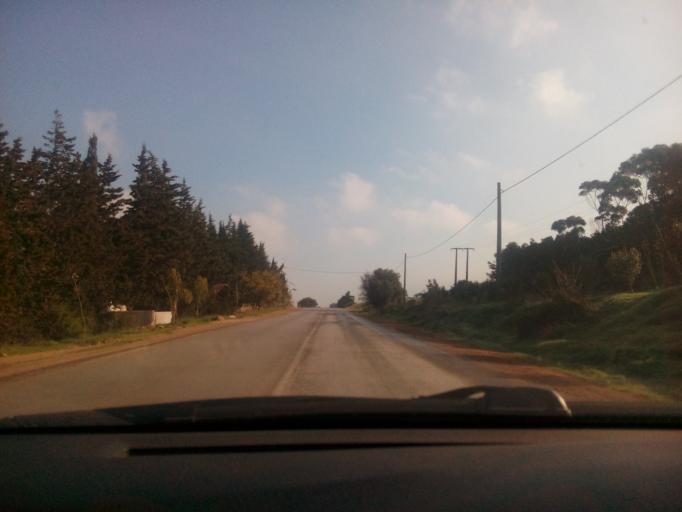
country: DZ
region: Oran
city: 'Ain el Turk
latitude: 35.7043
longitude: -0.8320
